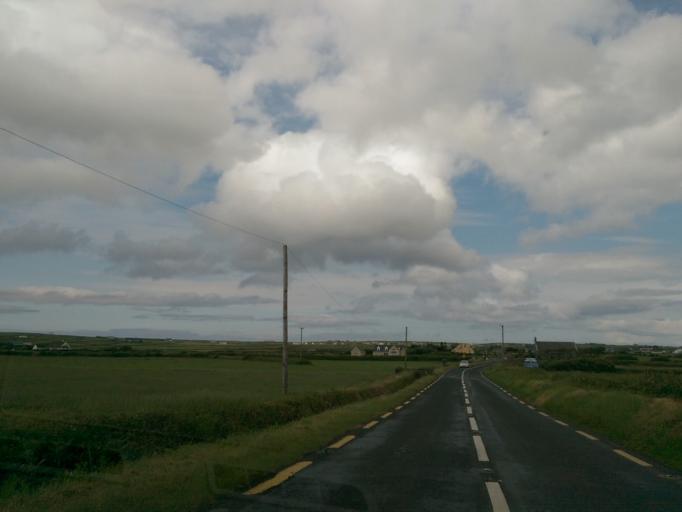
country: IE
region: Munster
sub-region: An Clar
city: Kilrush
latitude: 52.7111
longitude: -9.5914
